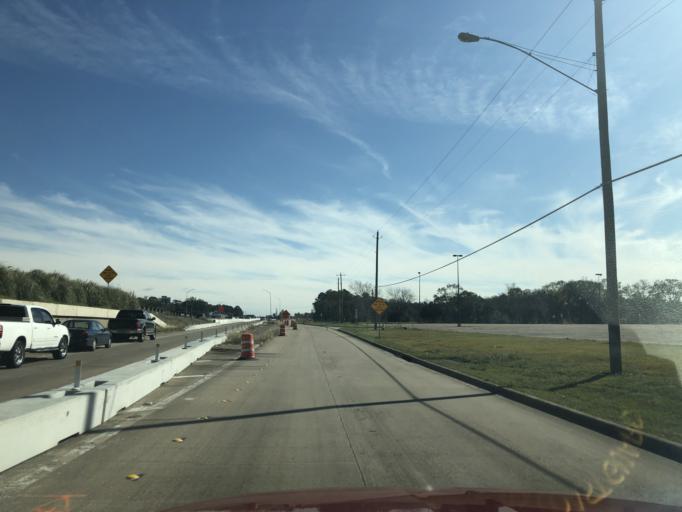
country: US
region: Texas
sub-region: Galveston County
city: Dickinson
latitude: 29.4476
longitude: -95.0763
